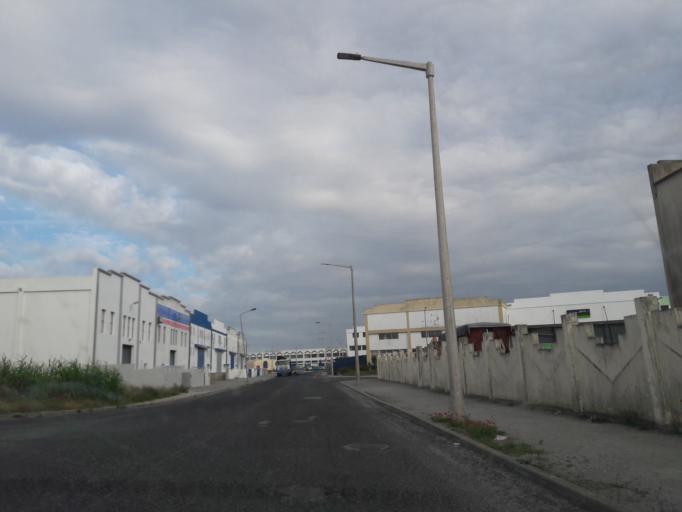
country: PT
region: Leiria
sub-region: Peniche
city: Peniche
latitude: 39.3601
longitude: -9.3753
